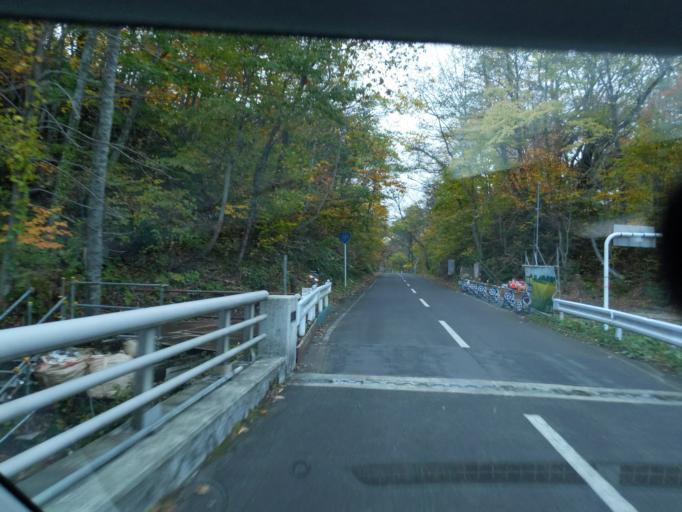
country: JP
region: Iwate
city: Mizusawa
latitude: 39.1090
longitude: 140.8582
